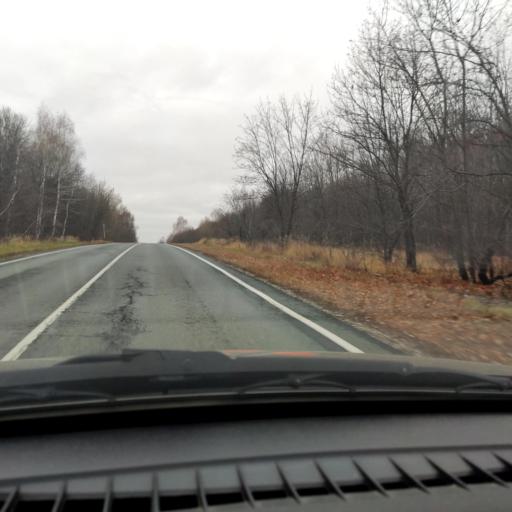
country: RU
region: Samara
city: Zhigulevsk
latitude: 53.3396
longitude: 49.4929
